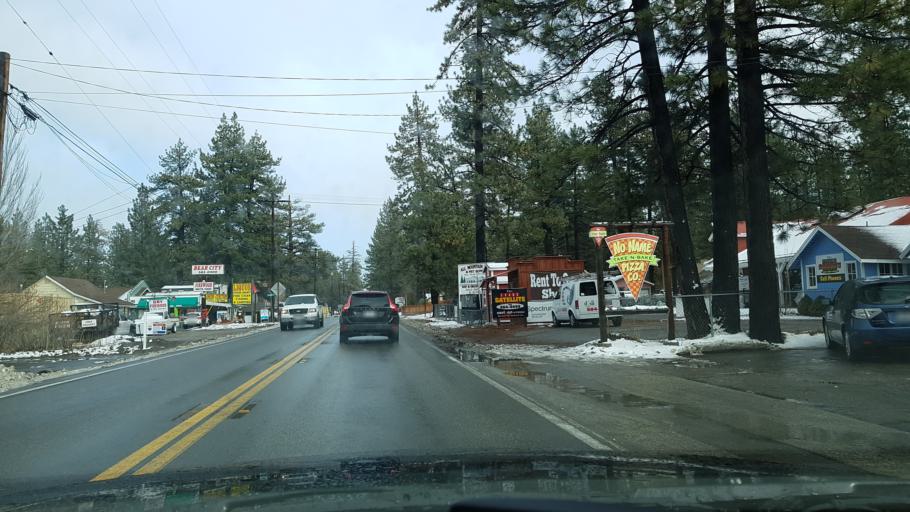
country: US
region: California
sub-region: San Bernardino County
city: Big Bear City
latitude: 34.2605
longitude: -116.8650
